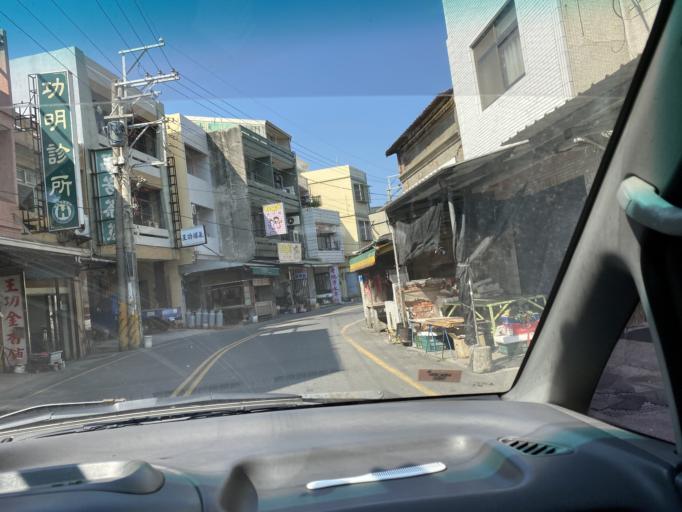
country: TW
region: Taiwan
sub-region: Changhua
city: Chang-hua
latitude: 23.9637
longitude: 120.3389
